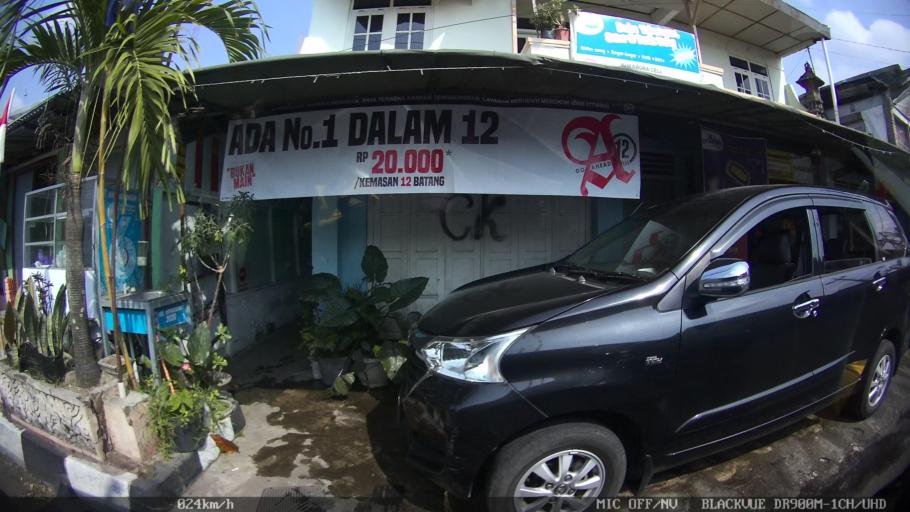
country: ID
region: Daerah Istimewa Yogyakarta
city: Yogyakarta
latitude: -7.8097
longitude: 110.3722
